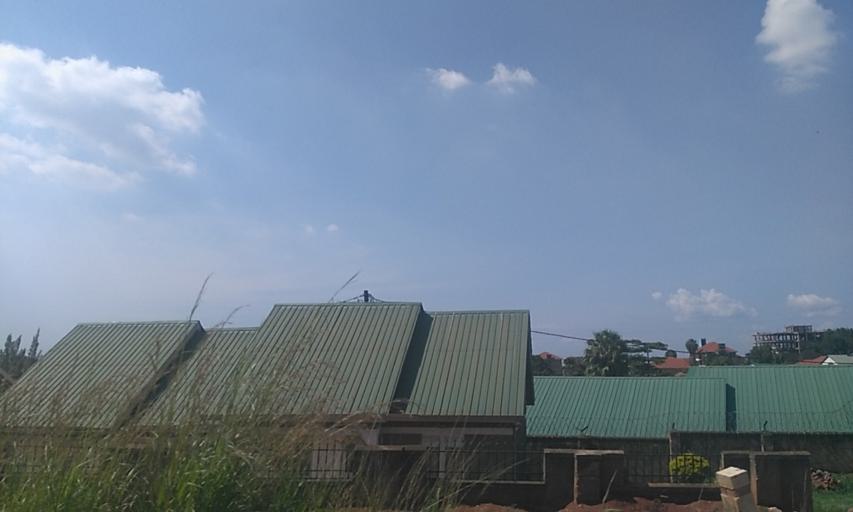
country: UG
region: Central Region
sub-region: Wakiso District
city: Kireka
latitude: 0.3626
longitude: 32.6389
